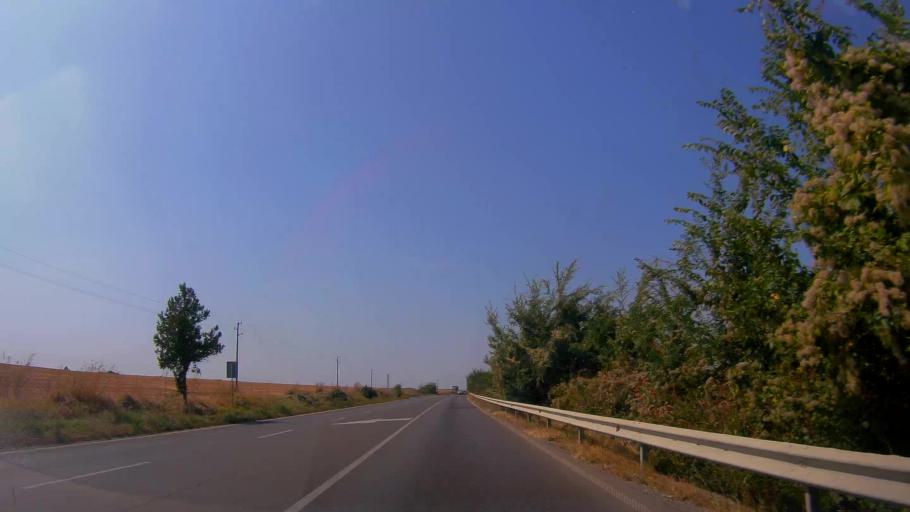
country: BG
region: Ruse
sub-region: Obshtina Vetovo
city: Senovo
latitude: 43.5621
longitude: 26.3486
